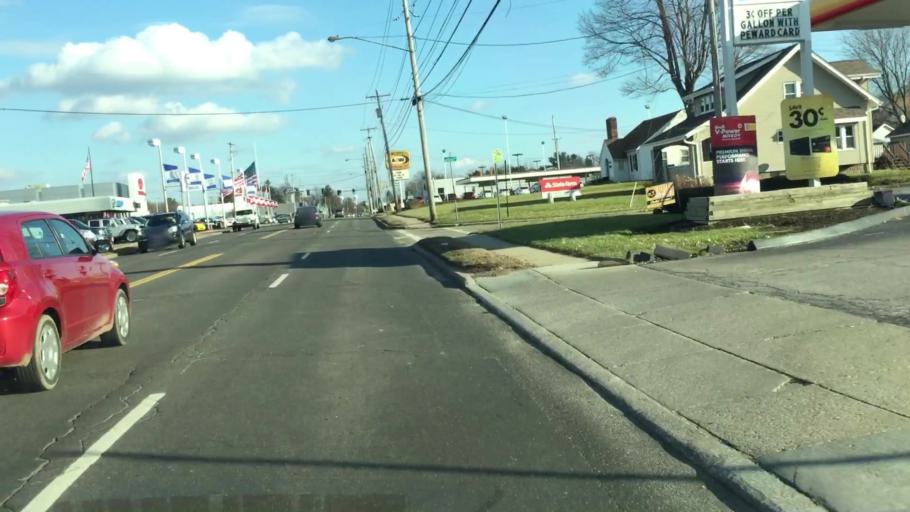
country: US
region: Ohio
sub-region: Portage County
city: Kent
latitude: 41.1516
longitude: -81.3840
